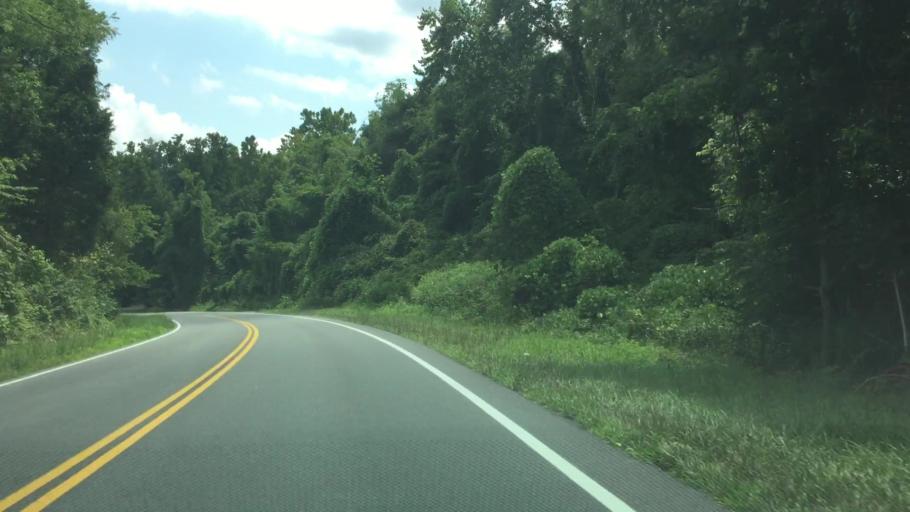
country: US
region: Virginia
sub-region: Pulaski County
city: Dublin
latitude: 37.0541
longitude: -80.7116
